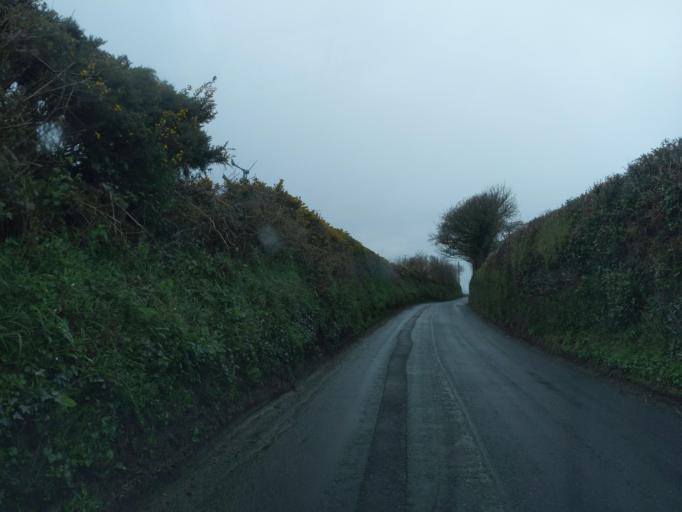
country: GB
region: England
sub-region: Cornwall
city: North Hill
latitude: 50.5831
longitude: -4.4329
